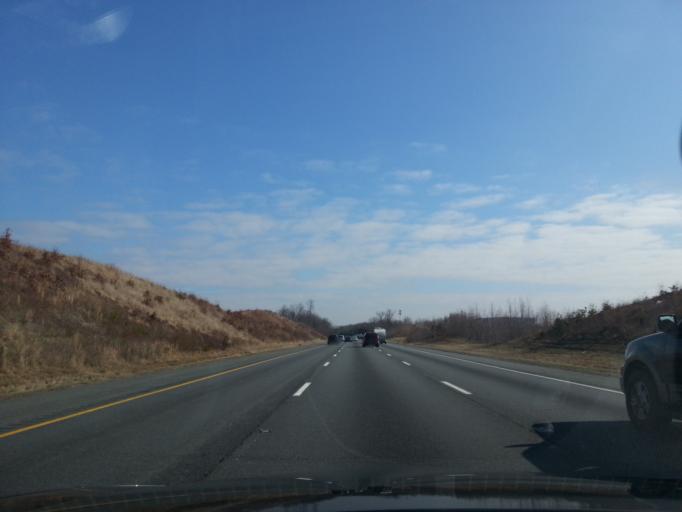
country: US
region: Virginia
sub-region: Stafford County
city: Stafford
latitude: 38.3878
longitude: -77.4447
